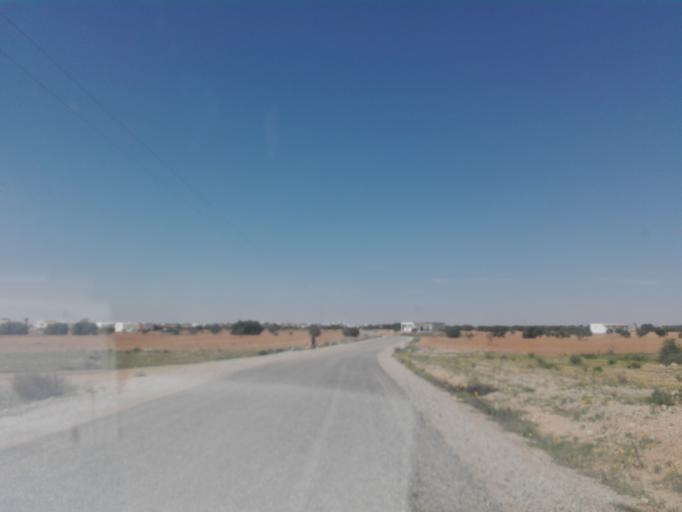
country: TN
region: Safaqis
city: Bi'r `Ali Bin Khalifah
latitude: 34.6705
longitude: 10.3679
